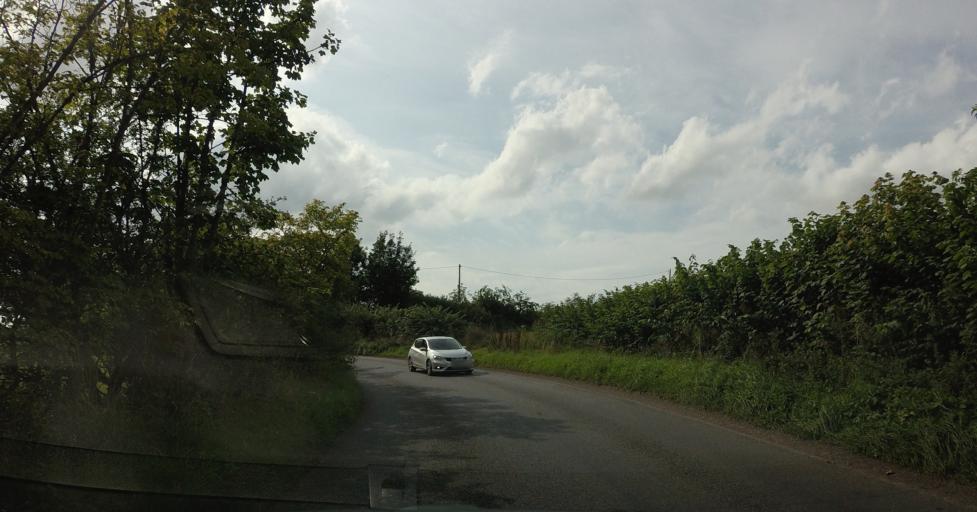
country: GB
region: Scotland
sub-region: Perth and Kinross
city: Methven
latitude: 56.3784
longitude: -3.6562
